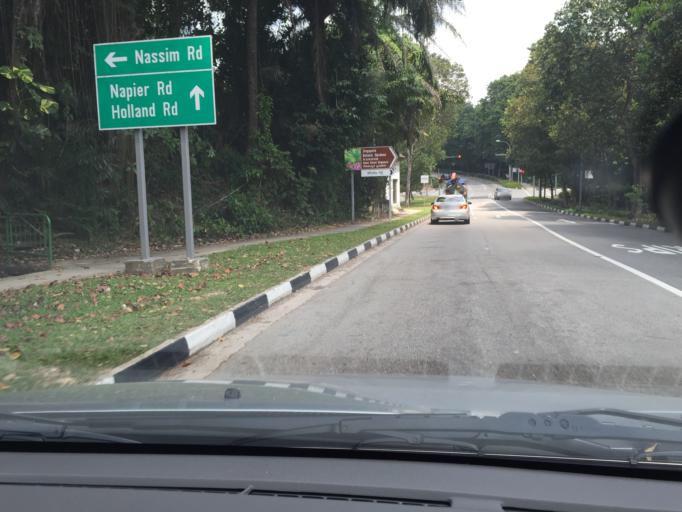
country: SG
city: Singapore
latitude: 1.3161
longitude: 103.8186
